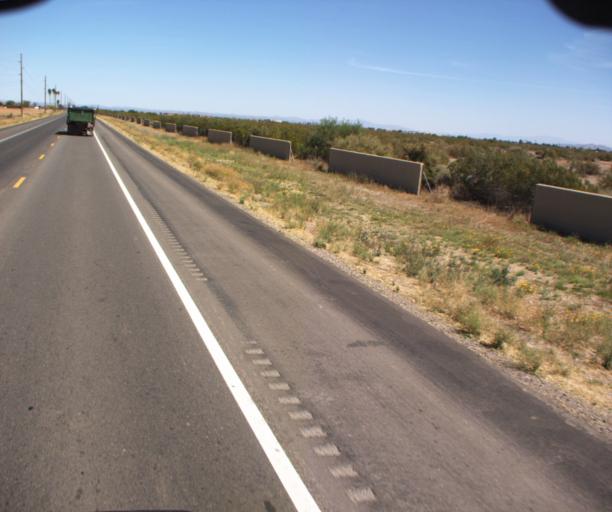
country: US
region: Arizona
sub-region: Pinal County
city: Coolidge
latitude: 33.0025
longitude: -111.5387
